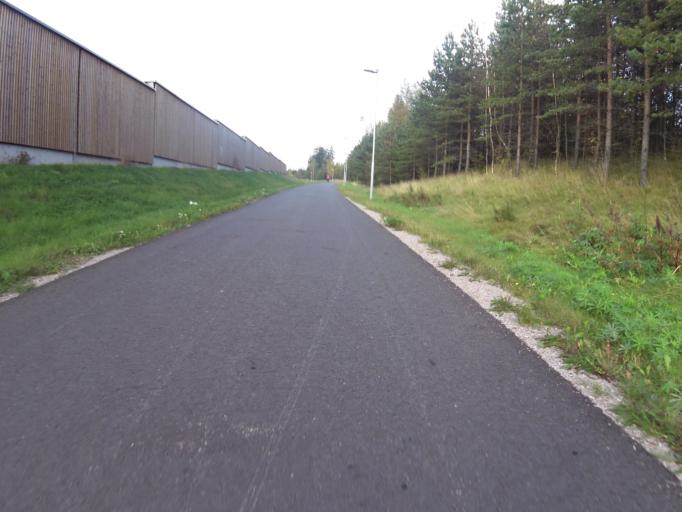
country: FI
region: Uusimaa
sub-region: Helsinki
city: Kauniainen
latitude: 60.2293
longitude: 24.6895
